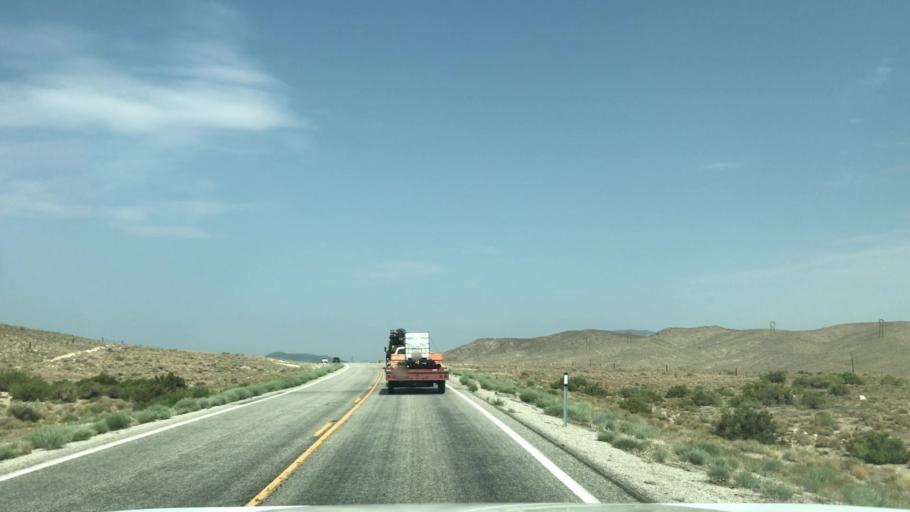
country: US
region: Nevada
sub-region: White Pine County
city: McGill
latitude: 39.0834
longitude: -114.1984
